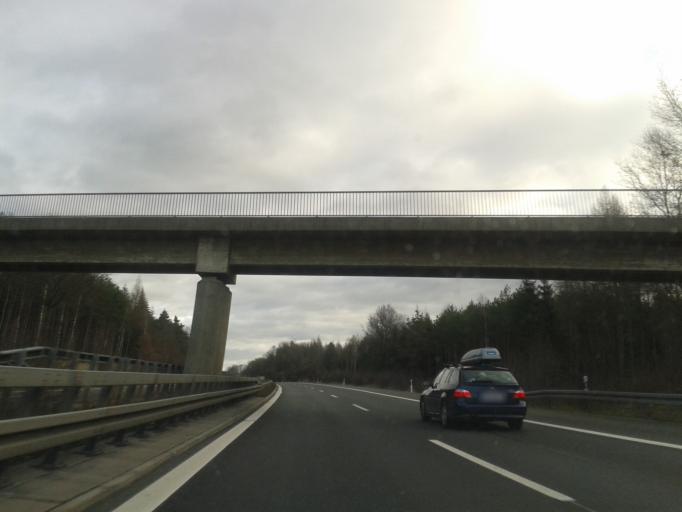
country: DE
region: Saxony
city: Grossrohrsdorf
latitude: 51.1541
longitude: 13.9910
